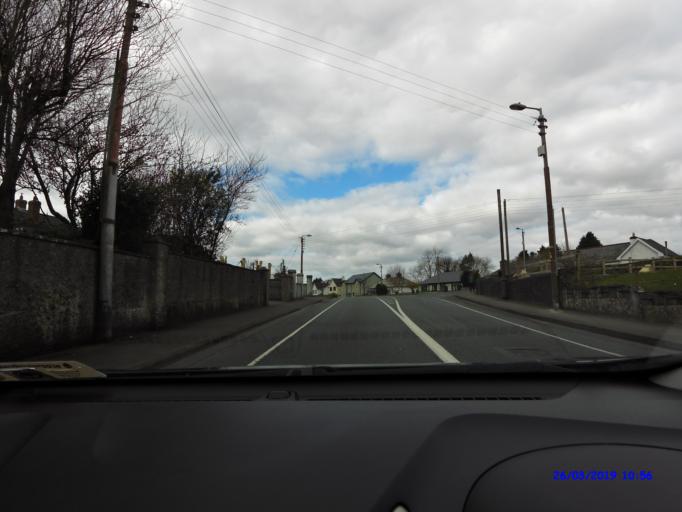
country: IE
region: Connaught
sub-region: Maigh Eo
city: Castlebar
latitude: 53.8579
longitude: -9.3098
